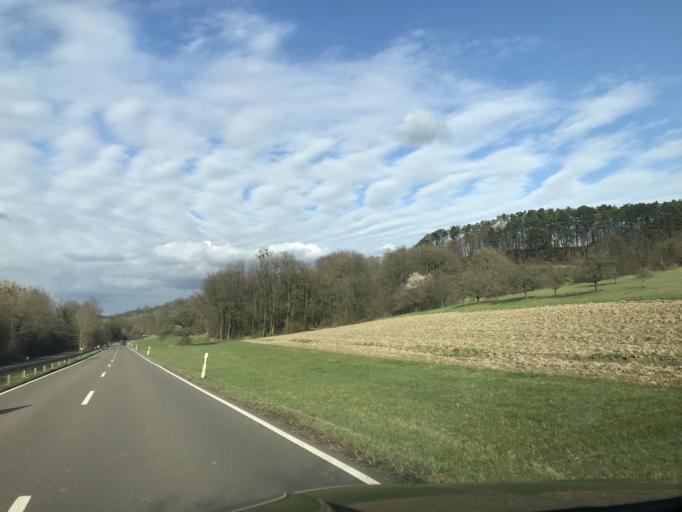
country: DE
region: Saarland
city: Gersheim
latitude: 49.1786
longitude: 7.2432
